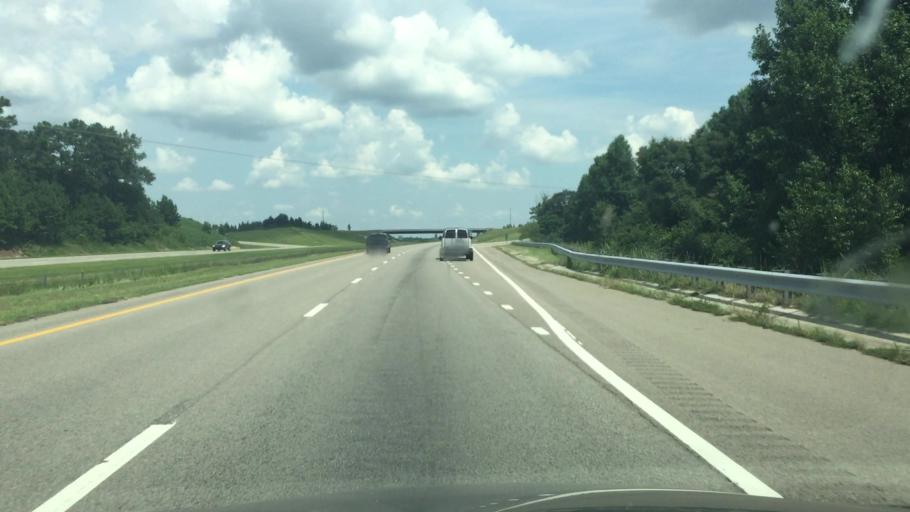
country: US
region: North Carolina
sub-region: Richmond County
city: Ellerbe
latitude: 35.1683
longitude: -79.7152
